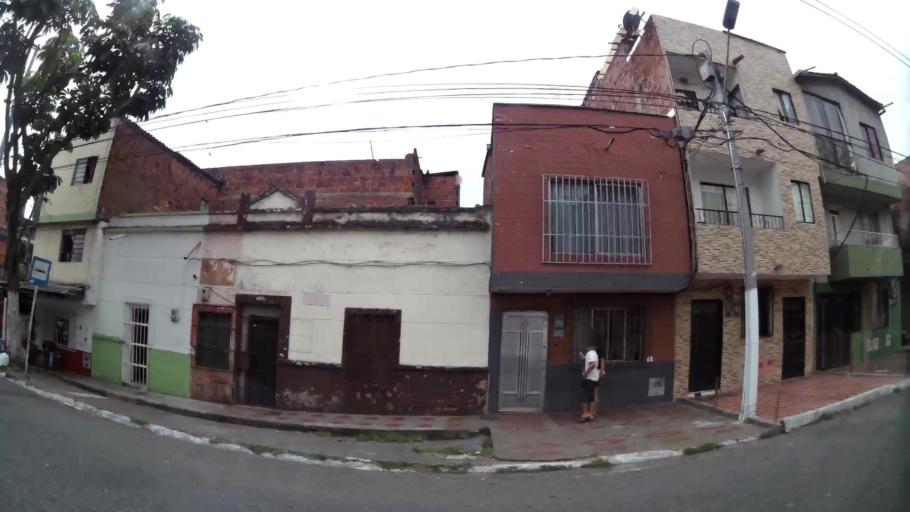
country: CO
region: Antioquia
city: Medellin
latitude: 6.2712
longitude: -75.5595
